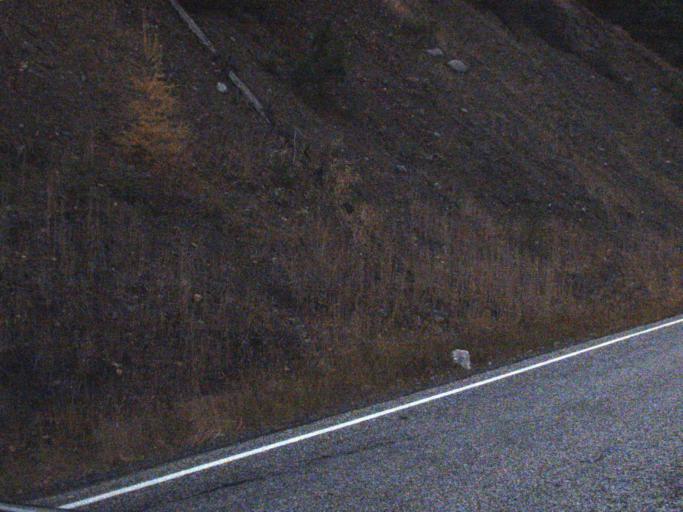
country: US
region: Washington
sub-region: Ferry County
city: Republic
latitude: 48.6142
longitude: -118.6649
